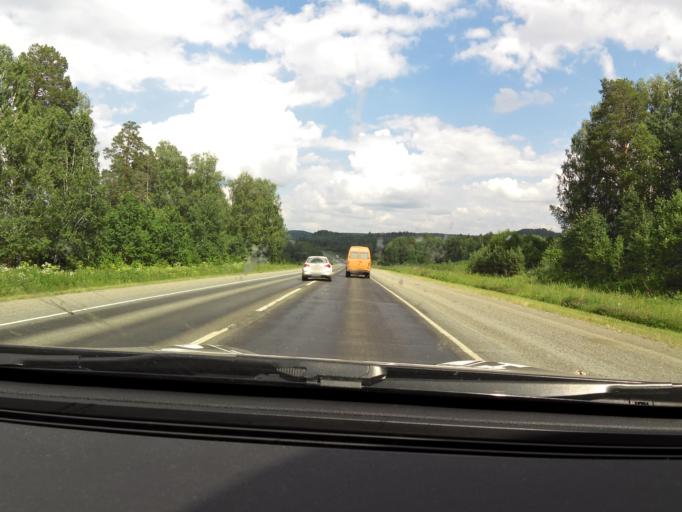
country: RU
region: Sverdlovsk
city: Bisert'
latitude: 56.8325
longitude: 58.8287
